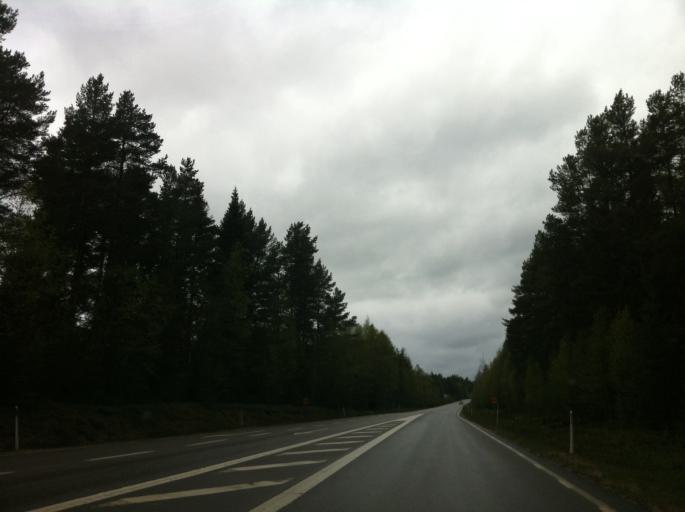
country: SE
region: Jaemtland
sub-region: Harjedalens Kommun
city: Sveg
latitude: 62.0463
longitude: 14.3420
